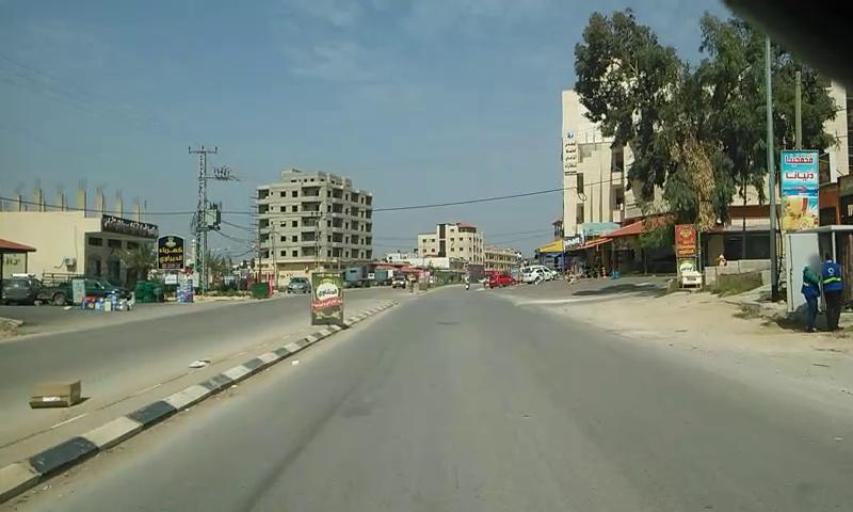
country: PS
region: West Bank
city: `Arranah
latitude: 32.4856
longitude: 35.2997
